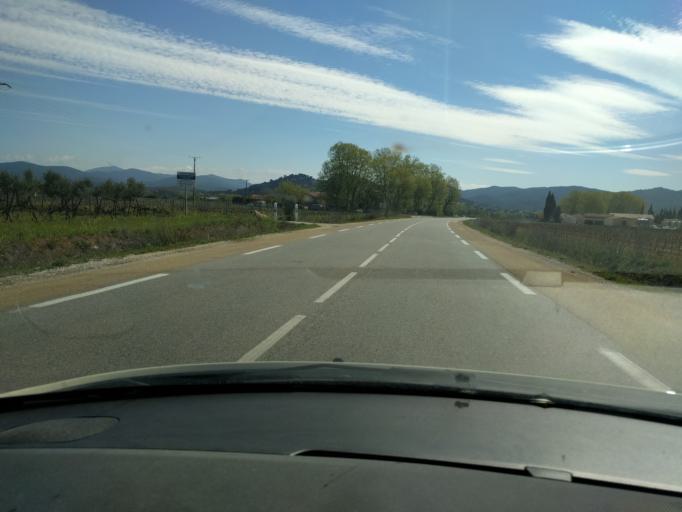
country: FR
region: Provence-Alpes-Cote d'Azur
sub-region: Departement du Var
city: Pierrefeu-du-Var
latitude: 43.2267
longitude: 6.1229
